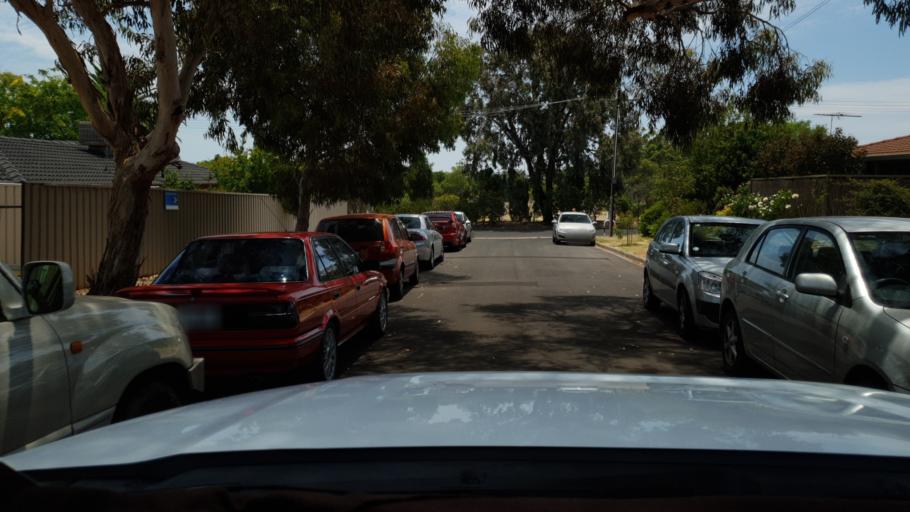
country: AU
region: South Australia
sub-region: Mitcham
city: Clapham
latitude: -35.0005
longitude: 138.5887
